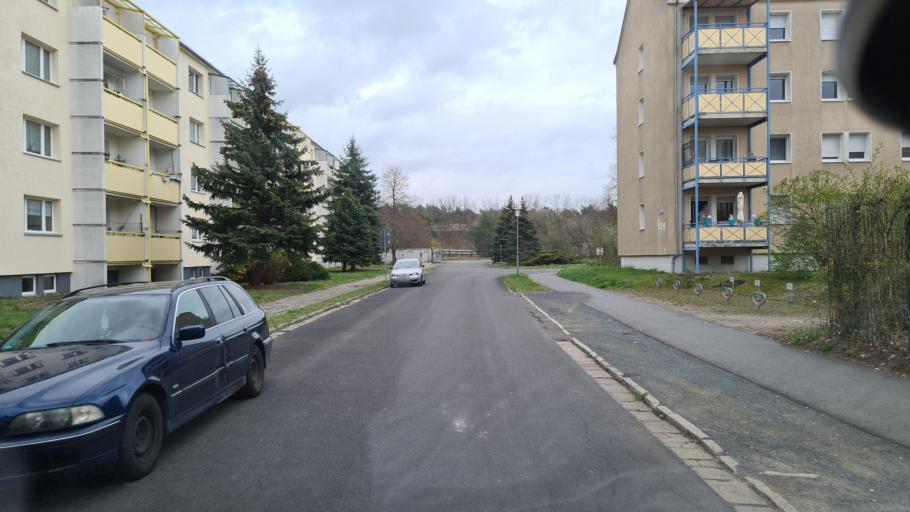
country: DE
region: Brandenburg
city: Schwarzheide
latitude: 51.4753
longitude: 13.8669
